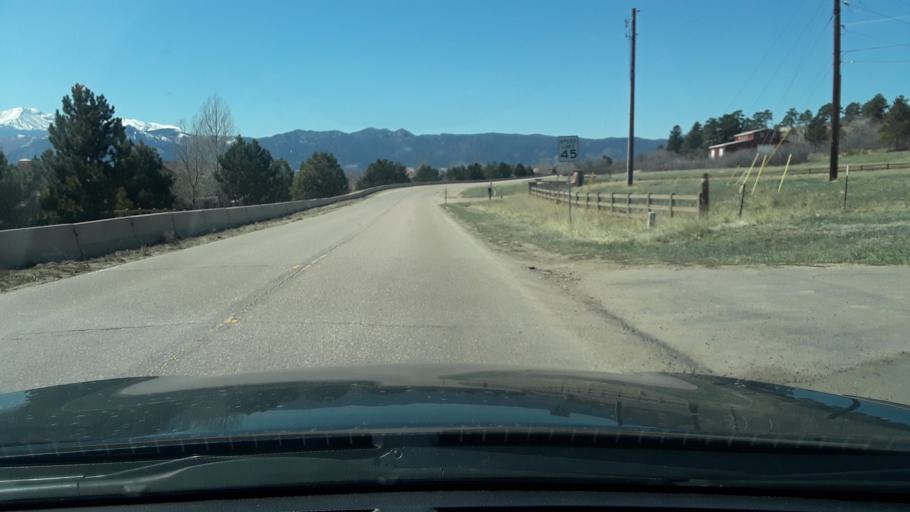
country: US
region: Colorado
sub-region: El Paso County
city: Gleneagle
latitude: 39.0350
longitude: -104.7776
